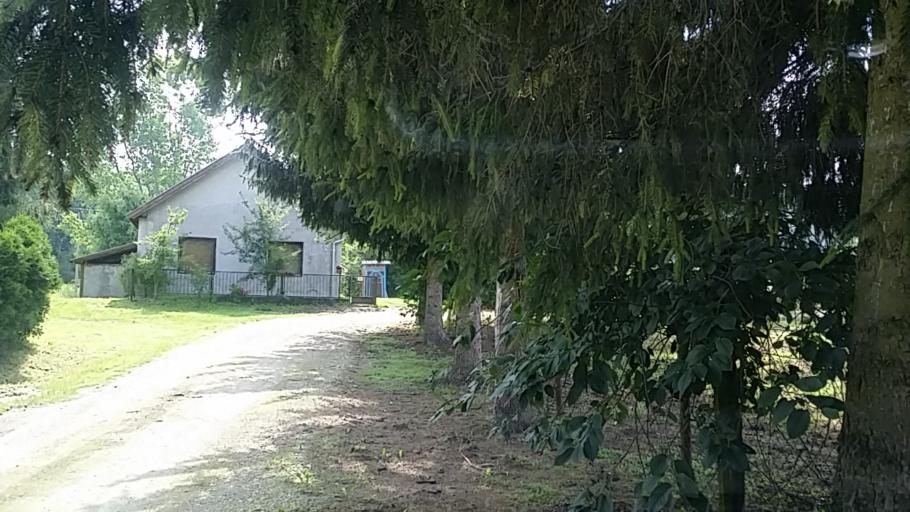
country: HU
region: Zala
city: Lenti
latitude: 46.5749
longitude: 16.5948
